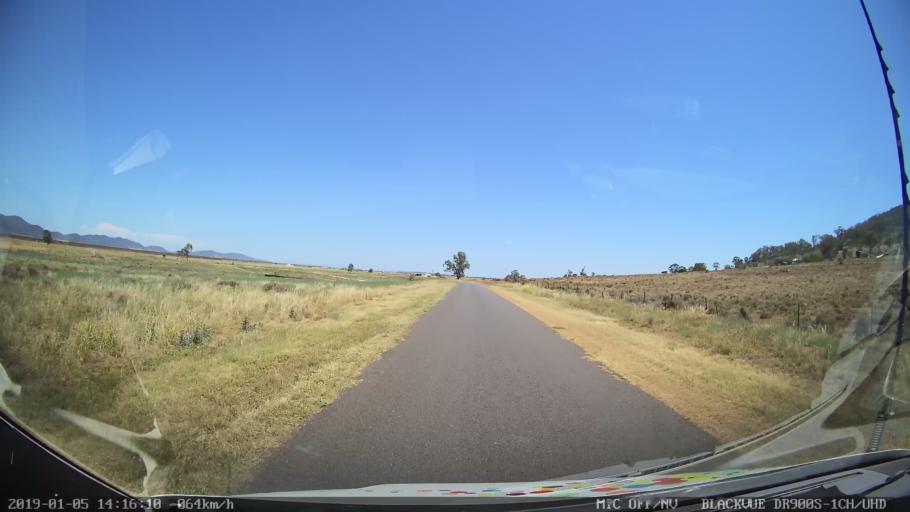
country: AU
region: New South Wales
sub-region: Liverpool Plains
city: Quirindi
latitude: -31.2541
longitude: 150.4724
